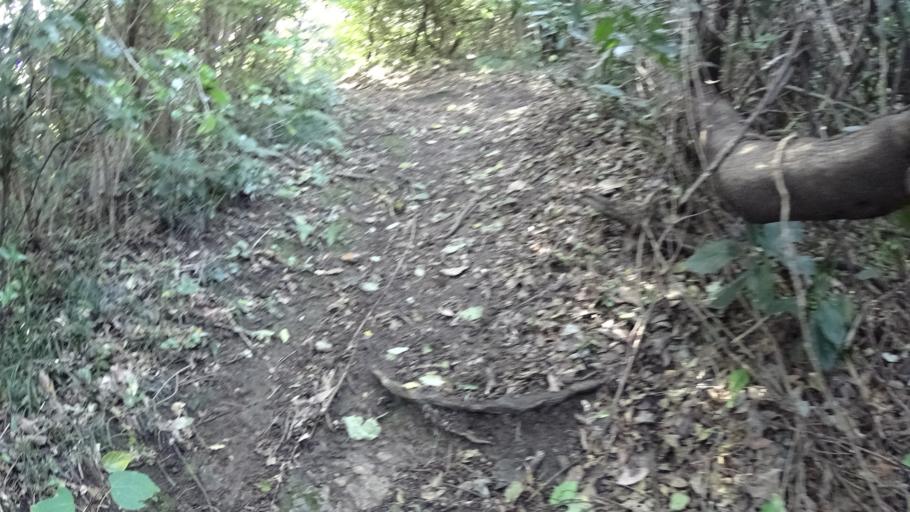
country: JP
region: Kanagawa
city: Yokosuka
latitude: 35.2758
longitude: 139.6230
